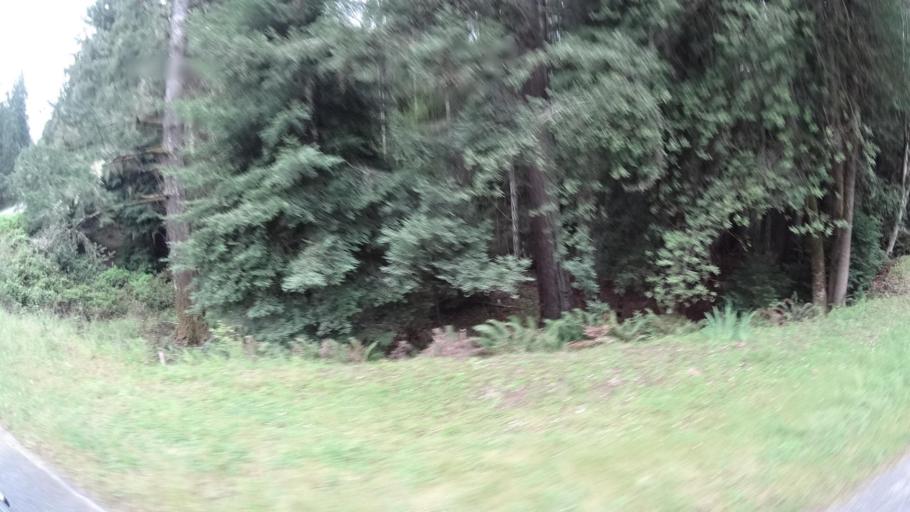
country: US
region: California
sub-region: Humboldt County
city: Redway
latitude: 40.2829
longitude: -123.7983
